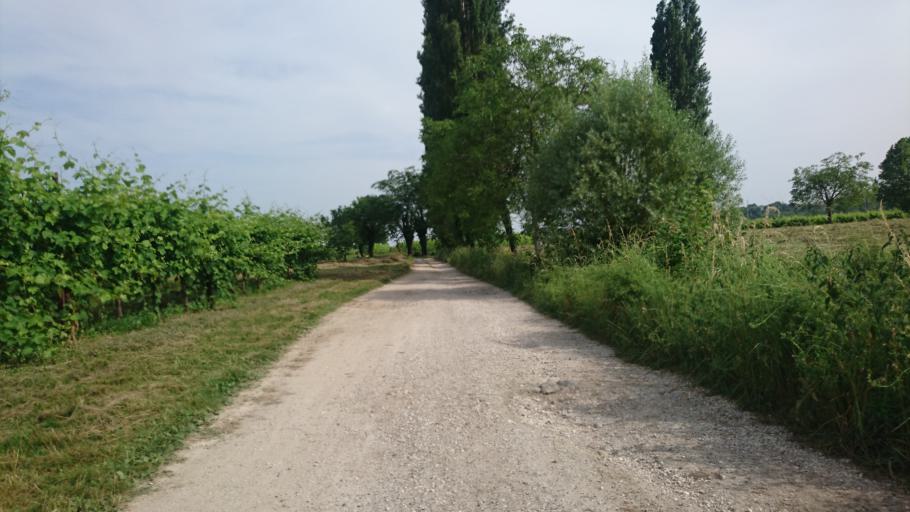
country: IT
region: Veneto
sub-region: Provincia di Treviso
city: Carpesica
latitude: 45.9633
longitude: 12.2962
